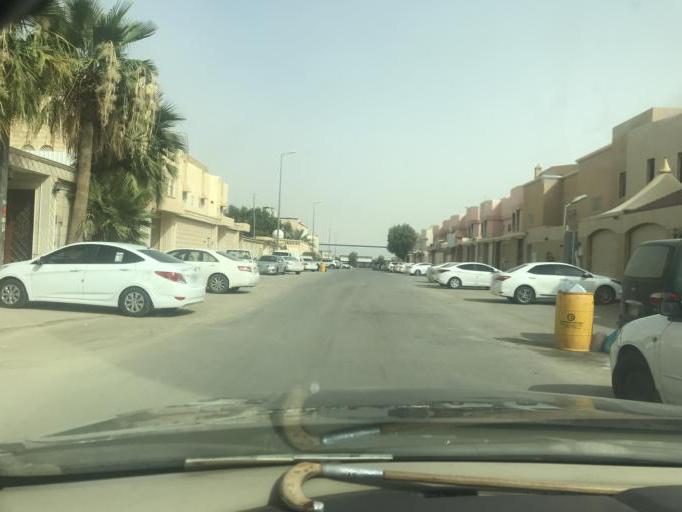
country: SA
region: Ar Riyad
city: Riyadh
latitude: 24.7566
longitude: 46.7685
